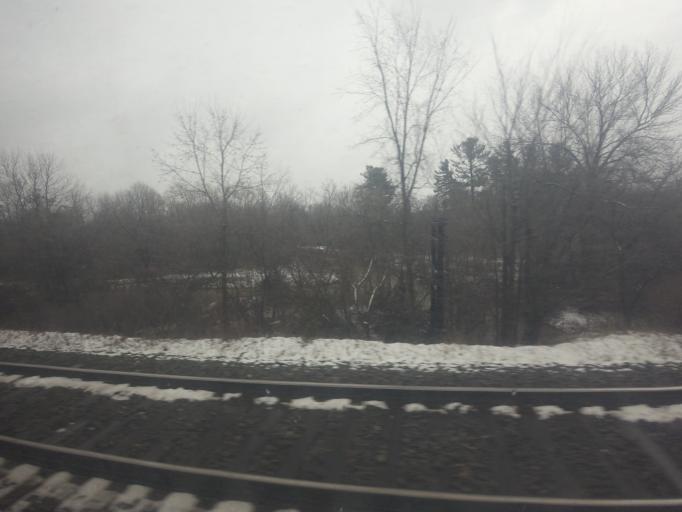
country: CA
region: Ontario
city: Quinte West
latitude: 44.1085
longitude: -77.6045
